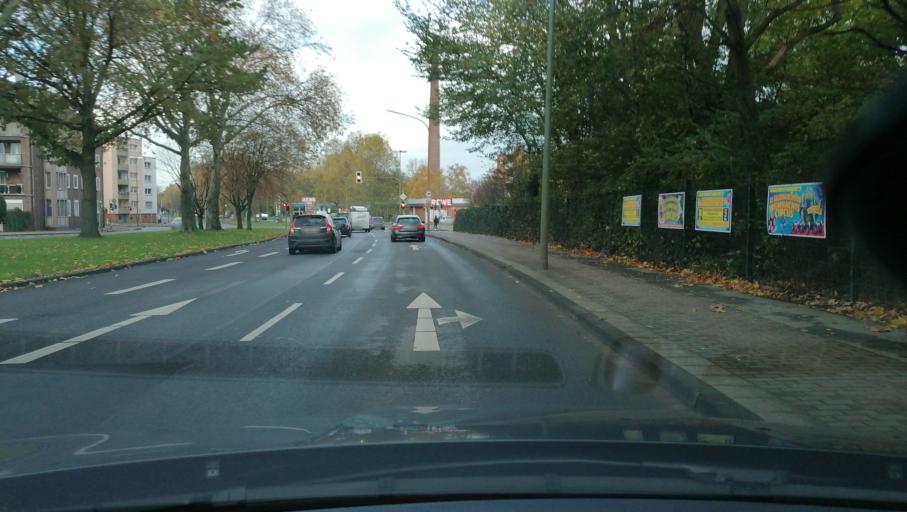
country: DE
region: North Rhine-Westphalia
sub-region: Regierungsbezirk Munster
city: Gelsenkirchen
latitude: 51.5182
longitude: 7.0848
